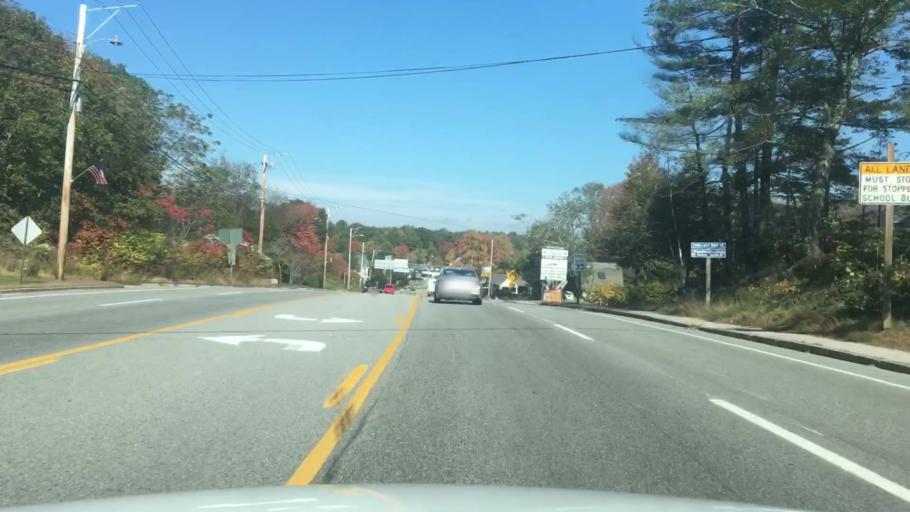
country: US
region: Maine
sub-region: Sagadahoc County
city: Woolwich
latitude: 43.9137
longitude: -69.8014
